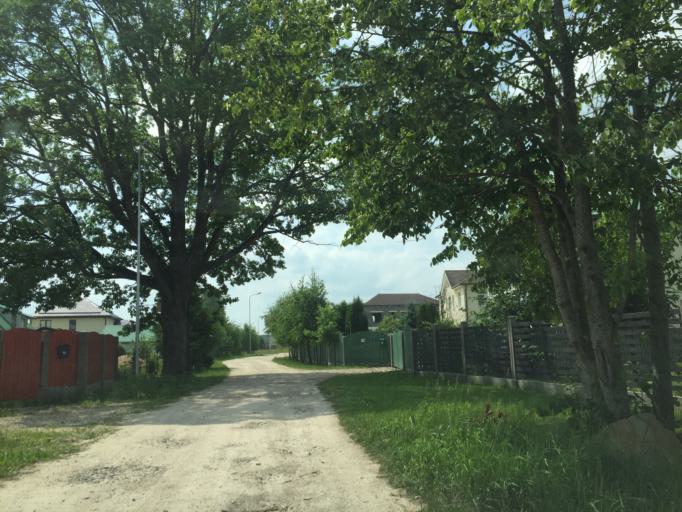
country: LV
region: Olaine
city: Olaine
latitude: 56.7779
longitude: 23.9243
